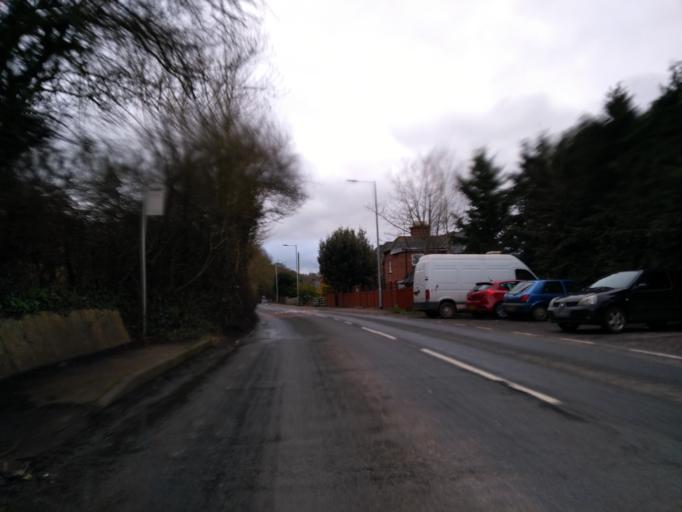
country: GB
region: England
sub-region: Devon
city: Exeter
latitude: 50.7644
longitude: -3.5082
